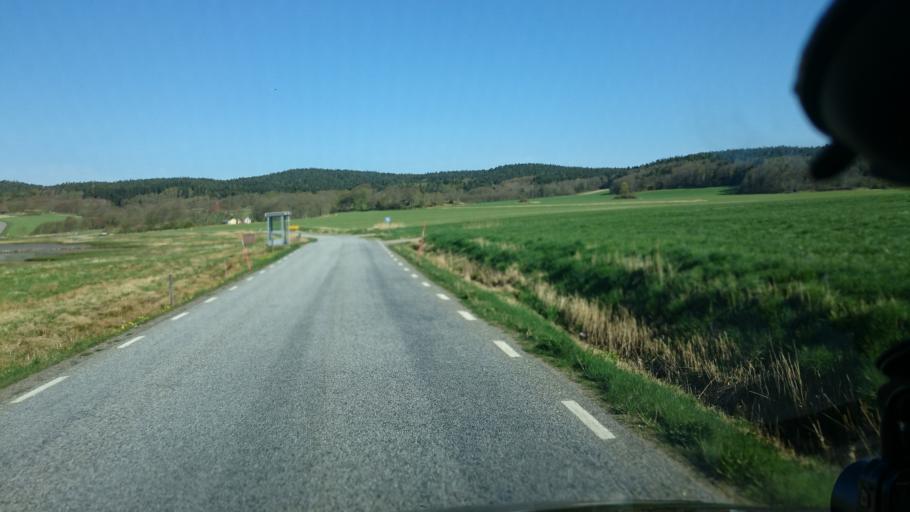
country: SE
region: Vaestra Goetaland
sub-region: Munkedals Kommun
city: Munkedal
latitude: 58.3894
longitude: 11.6594
